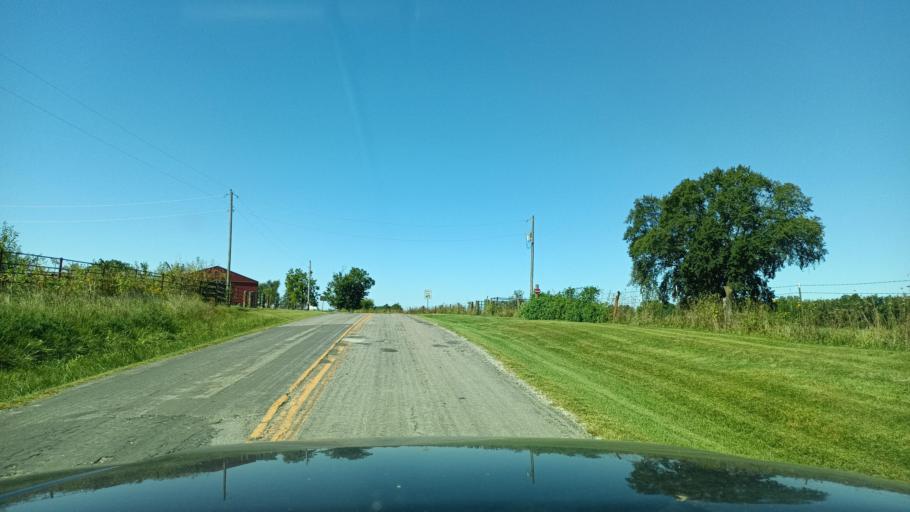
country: US
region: Missouri
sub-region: Scotland County
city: Memphis
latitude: 40.3539
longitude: -92.2987
